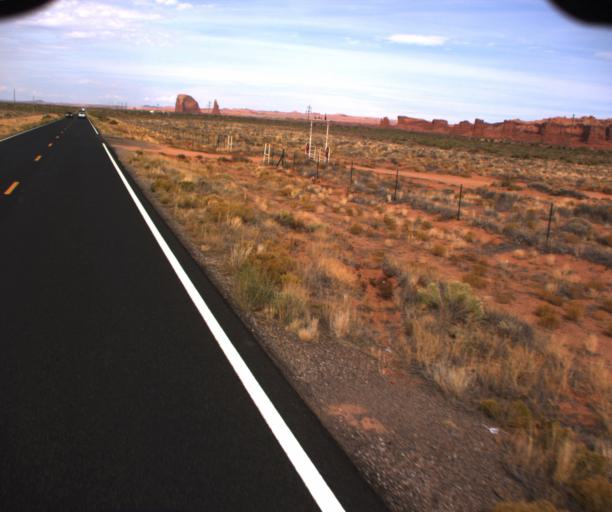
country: US
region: Arizona
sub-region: Apache County
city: Many Farms
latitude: 36.6179
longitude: -109.5805
